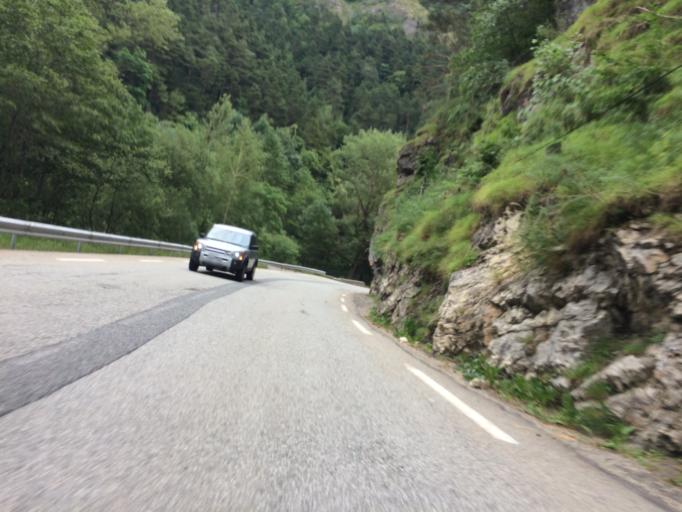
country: FR
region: Provence-Alpes-Cote d'Azur
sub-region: Departement des Alpes-Maritimes
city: Tende
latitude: 44.1288
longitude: 7.5660
